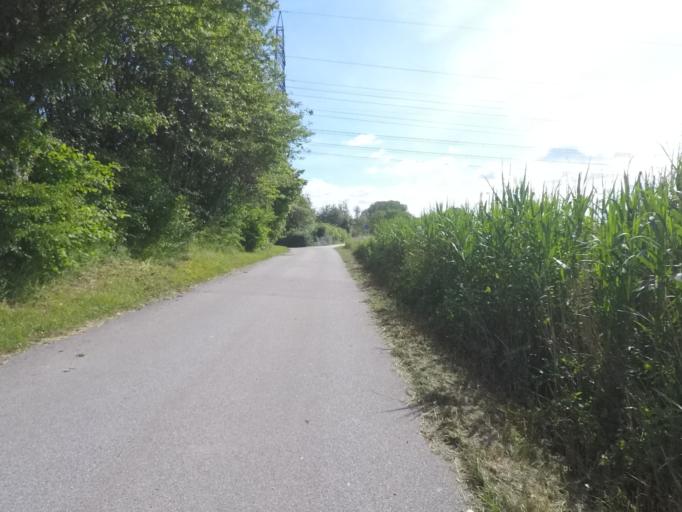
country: SE
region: Skane
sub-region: Malmo
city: Oxie
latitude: 55.5847
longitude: 13.1408
